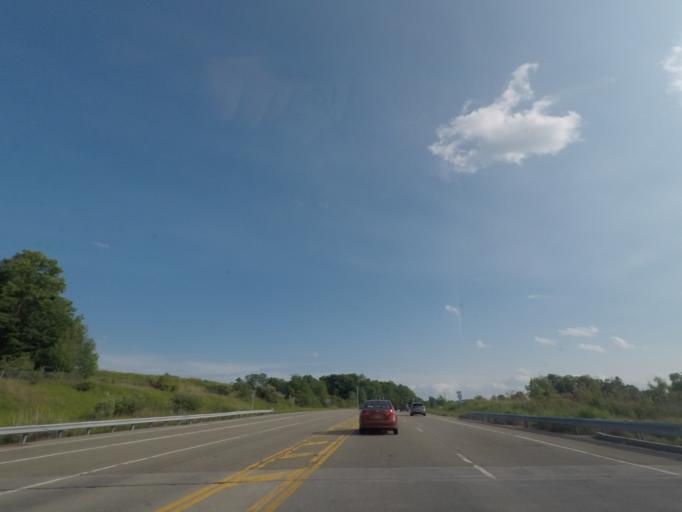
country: US
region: New York
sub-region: Orange County
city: Orange Lake
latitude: 41.5123
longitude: -74.1305
